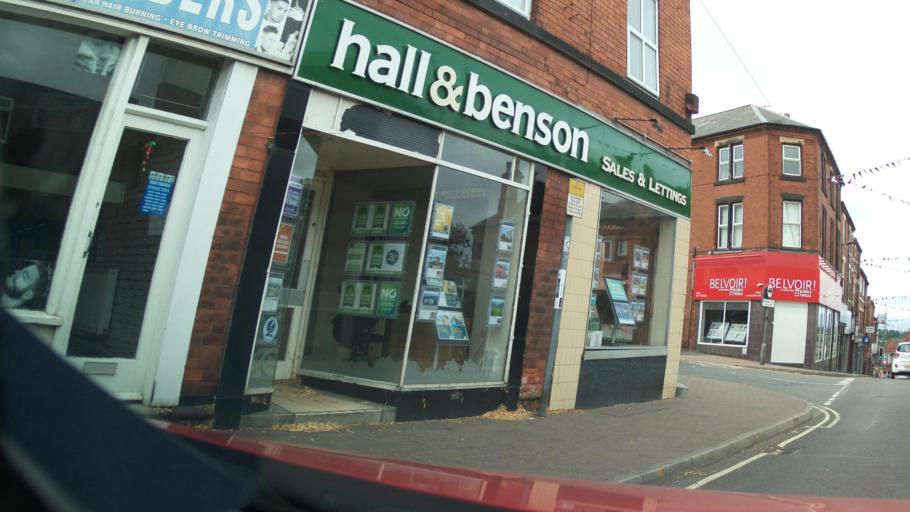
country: GB
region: England
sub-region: Derbyshire
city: Heanor
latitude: 53.0141
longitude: -1.3546
